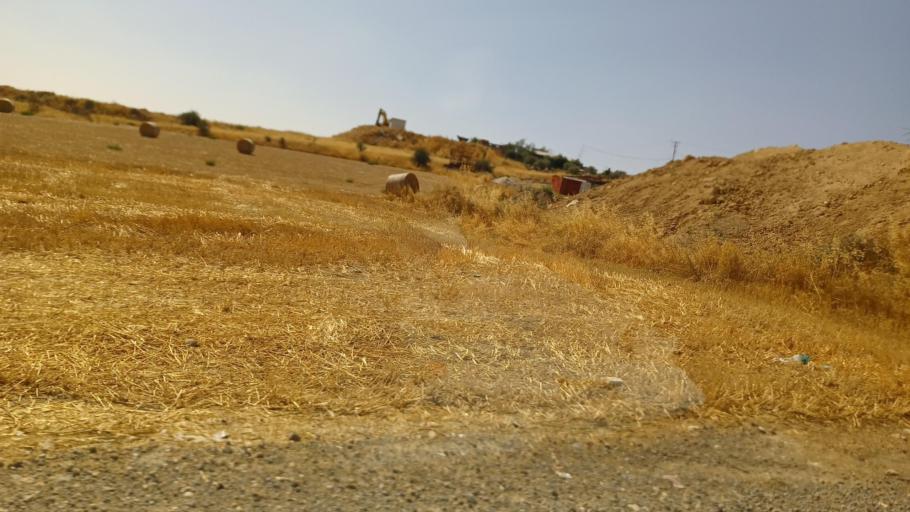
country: CY
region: Larnaka
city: Athienou
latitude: 35.0460
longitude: 33.5357
